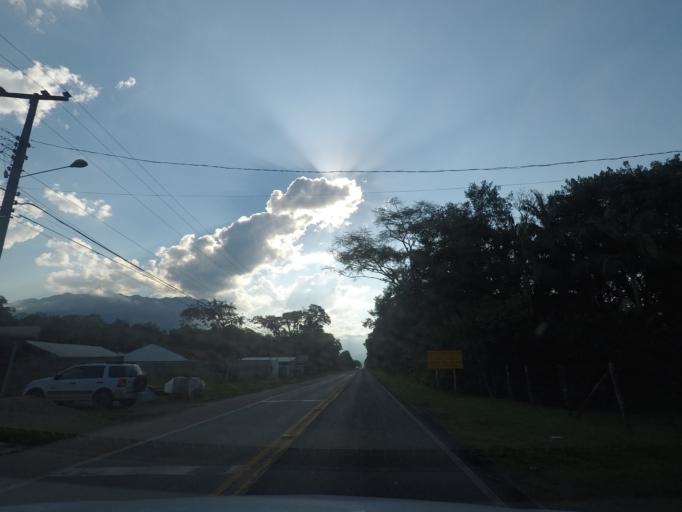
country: BR
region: Parana
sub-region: Antonina
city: Antonina
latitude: -25.4716
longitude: -48.8409
